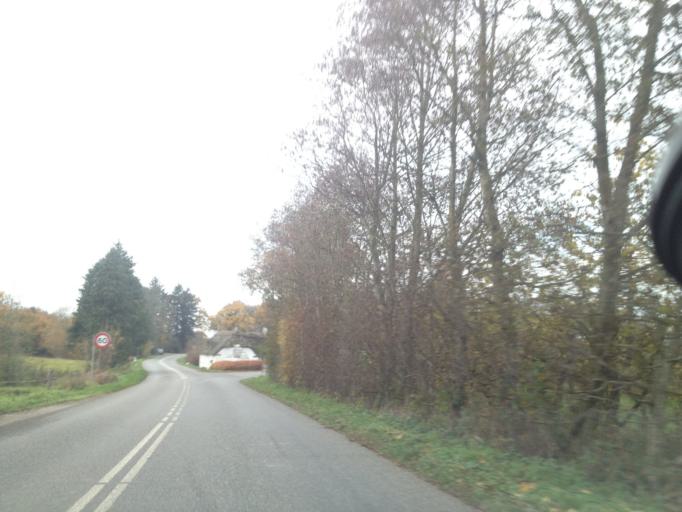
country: DK
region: South Denmark
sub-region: Assens Kommune
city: Vissenbjerg
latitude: 55.4106
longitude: 10.1537
